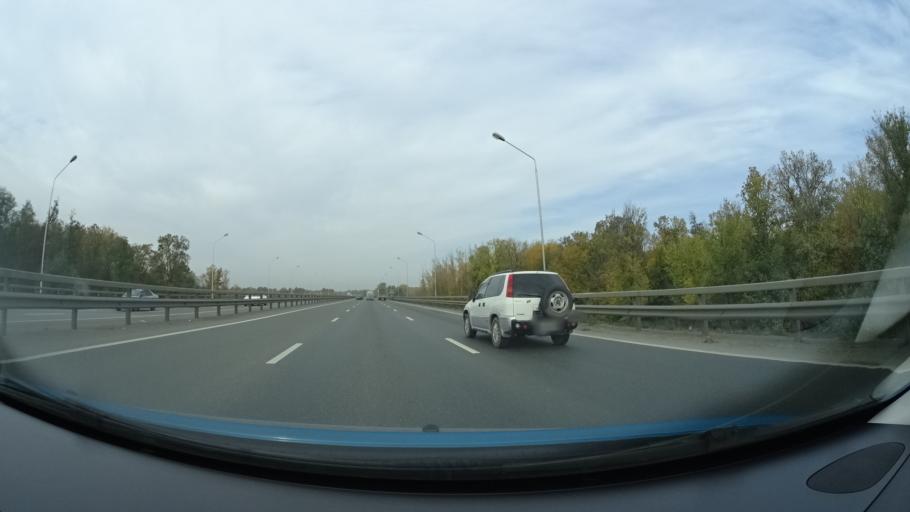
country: RU
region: Bashkortostan
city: Ufa
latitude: 54.6533
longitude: 55.9011
